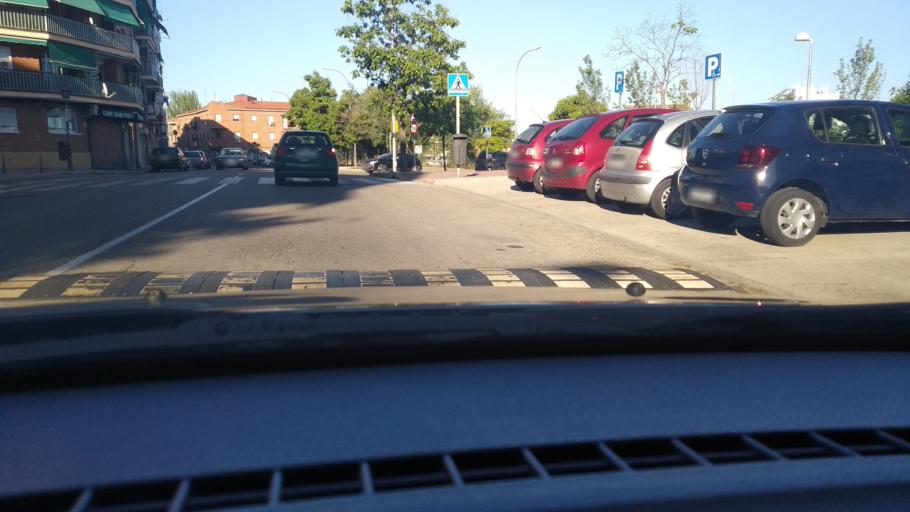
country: ES
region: Madrid
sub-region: Provincia de Madrid
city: Villa de Vallecas
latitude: 40.3773
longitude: -3.6270
